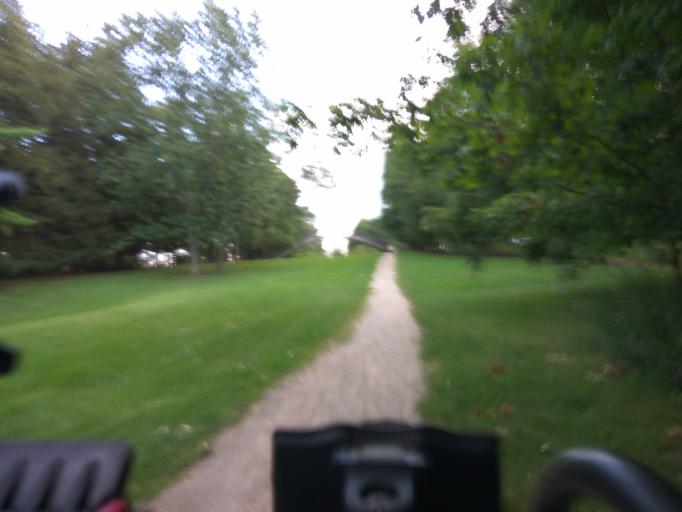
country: CA
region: Ontario
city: Stratford
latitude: 43.3754
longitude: -80.9643
